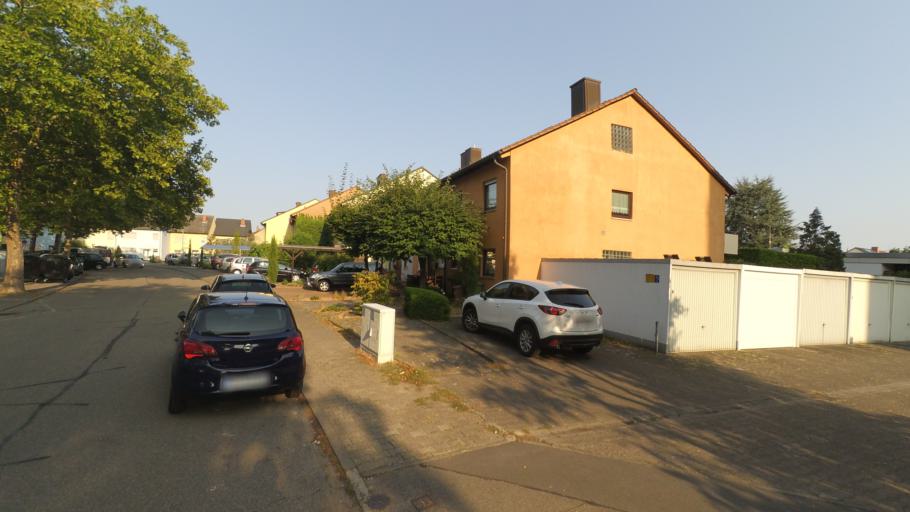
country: DE
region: Hesse
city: Viernheim
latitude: 49.5419
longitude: 8.5917
